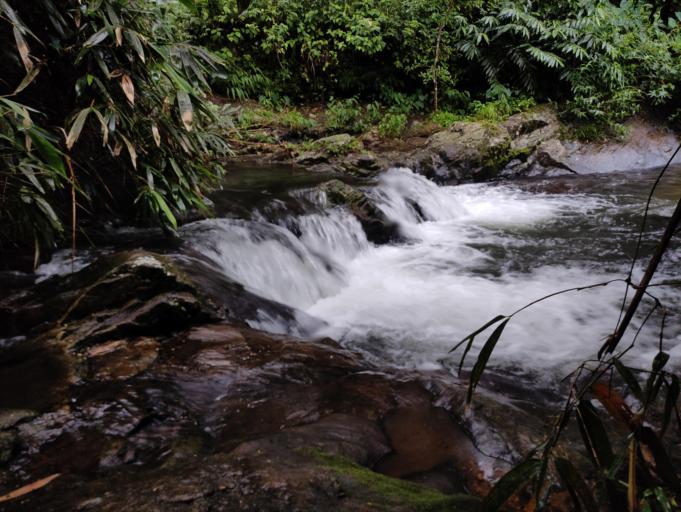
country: IN
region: Kerala
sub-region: Kottayam
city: Erattupetta
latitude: 9.7748
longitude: 76.8098
